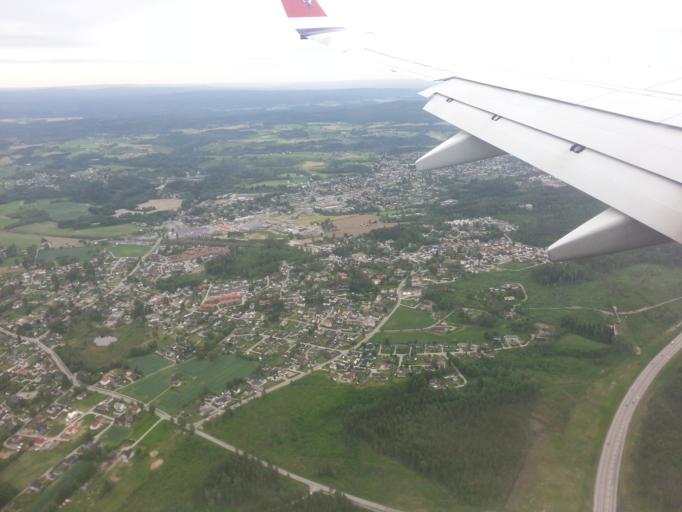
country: NO
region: Akershus
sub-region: Eidsvoll
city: Raholt
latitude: 60.2872
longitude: 11.1356
